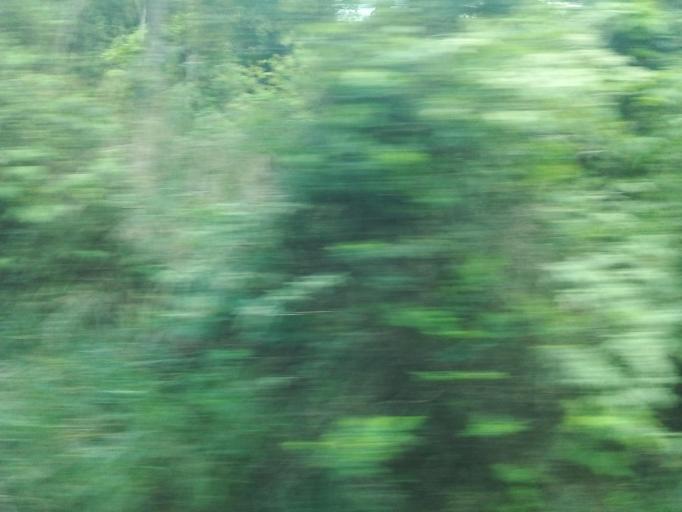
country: BR
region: Minas Gerais
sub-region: Rio Piracicaba
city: Rio Piracicaba
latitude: -19.8880
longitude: -43.1319
